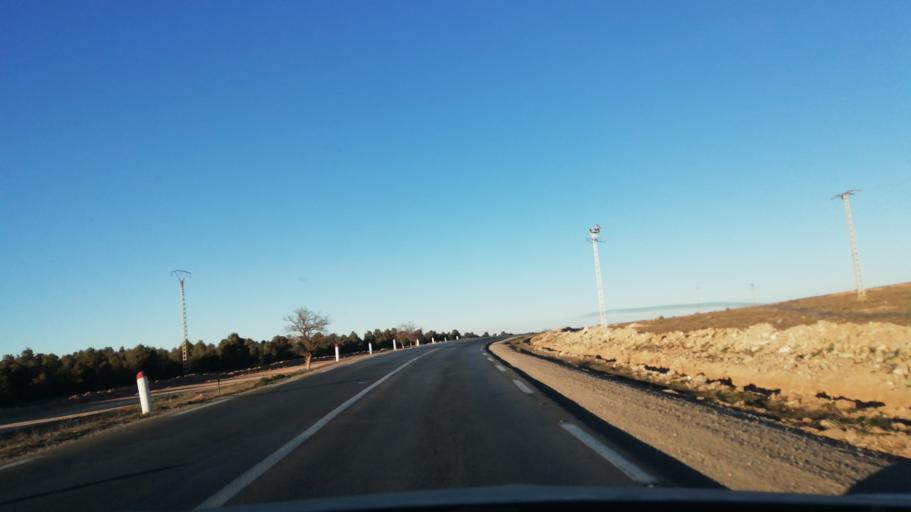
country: DZ
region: Saida
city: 'Ain el Hadjar
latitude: 34.5608
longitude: 0.1190
